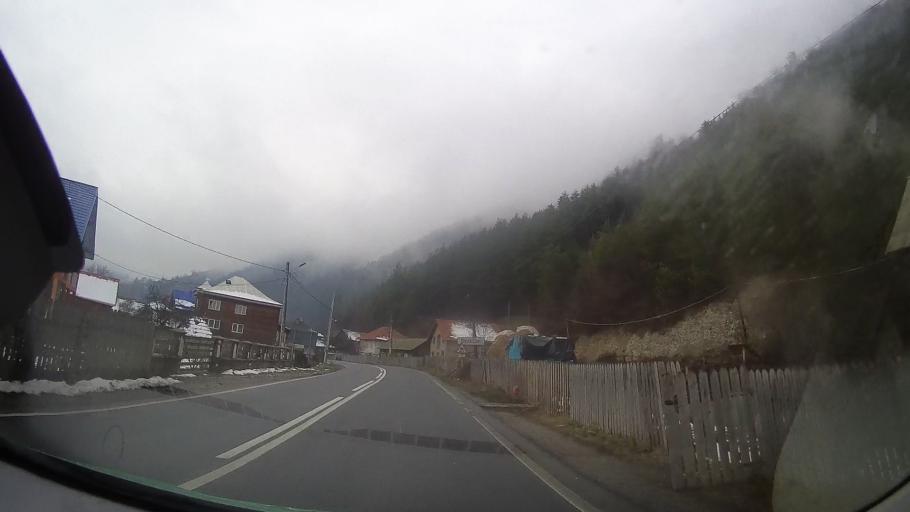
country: RO
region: Neamt
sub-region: Comuna Bicaz Chei
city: Bicaz Chei
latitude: 46.8424
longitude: 25.8972
